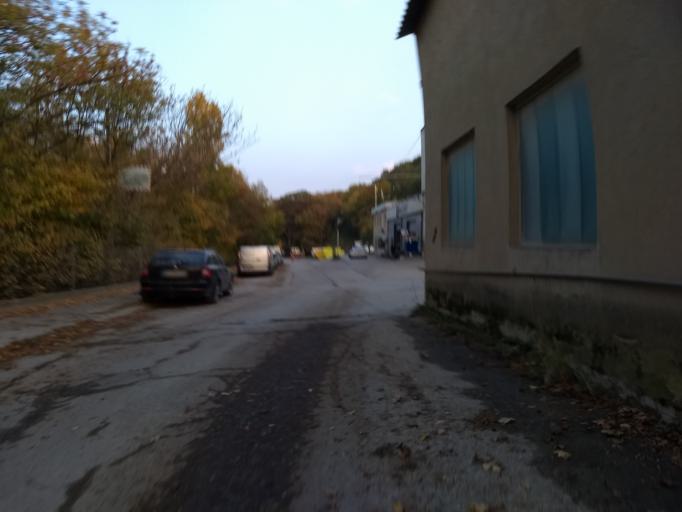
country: AT
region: Lower Austria
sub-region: Politischer Bezirk Modling
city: Perchtoldsdorf
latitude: 48.1303
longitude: 16.2393
